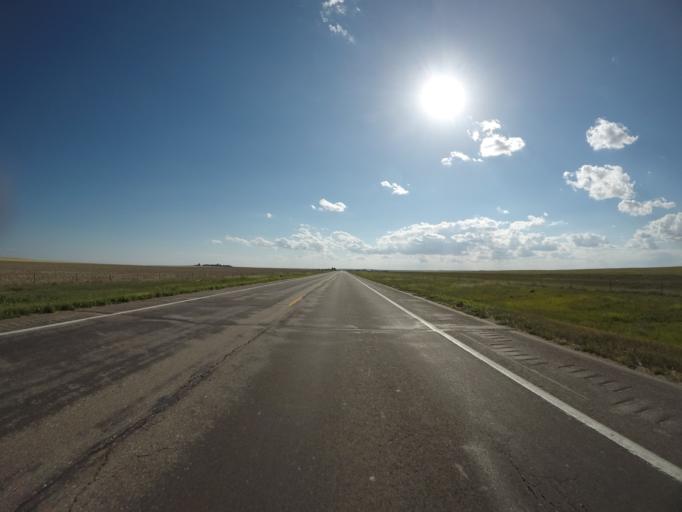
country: US
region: Colorado
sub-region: Morgan County
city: Fort Morgan
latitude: 40.6020
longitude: -103.8603
